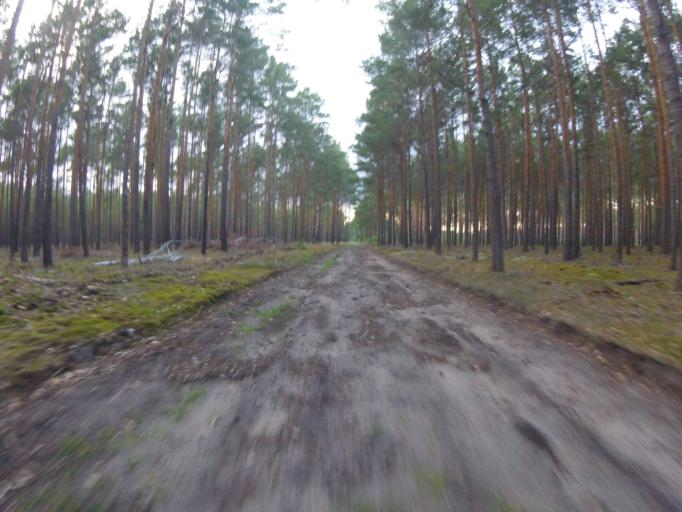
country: DE
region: Brandenburg
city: Gross Koris
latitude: 52.2091
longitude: 13.6754
